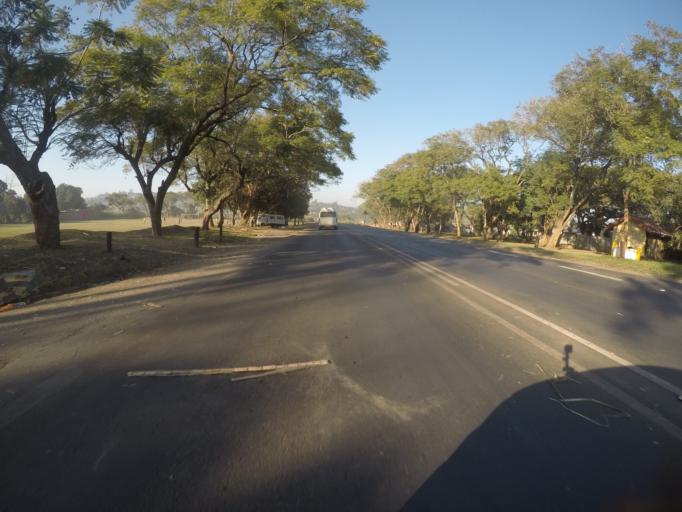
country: ZA
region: KwaZulu-Natal
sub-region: iLembe District Municipality
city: Stanger
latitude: -29.3789
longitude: 31.2525
